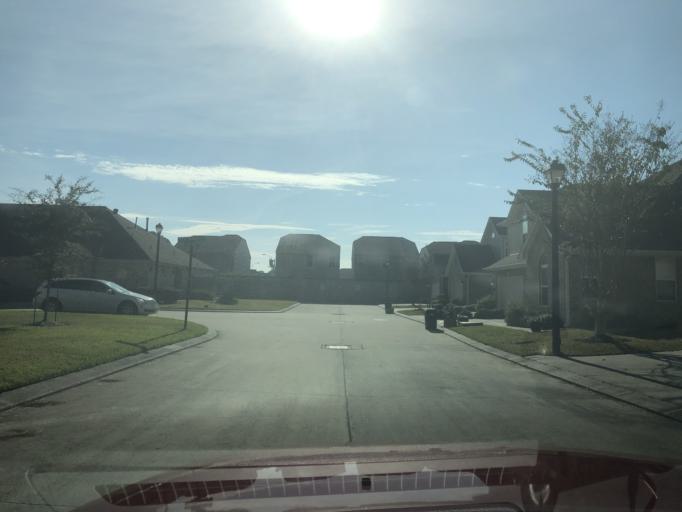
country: US
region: Texas
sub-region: Harris County
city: Spring
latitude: 30.0122
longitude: -95.4628
